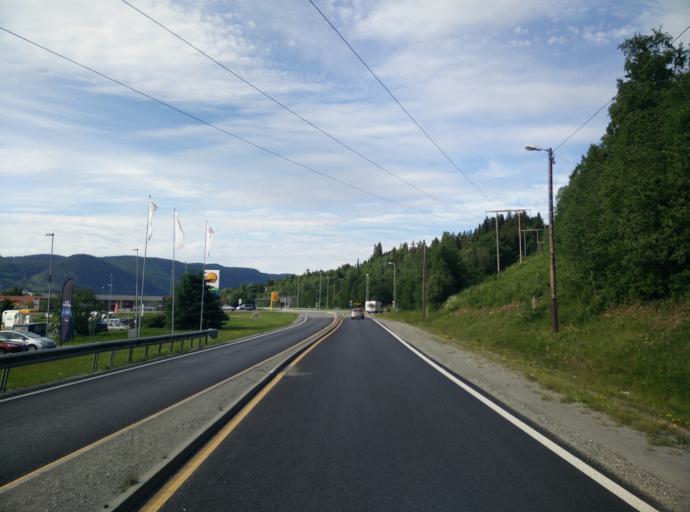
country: NO
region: Sor-Trondelag
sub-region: Orkdal
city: Orkanger
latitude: 63.2952
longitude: 9.8535
